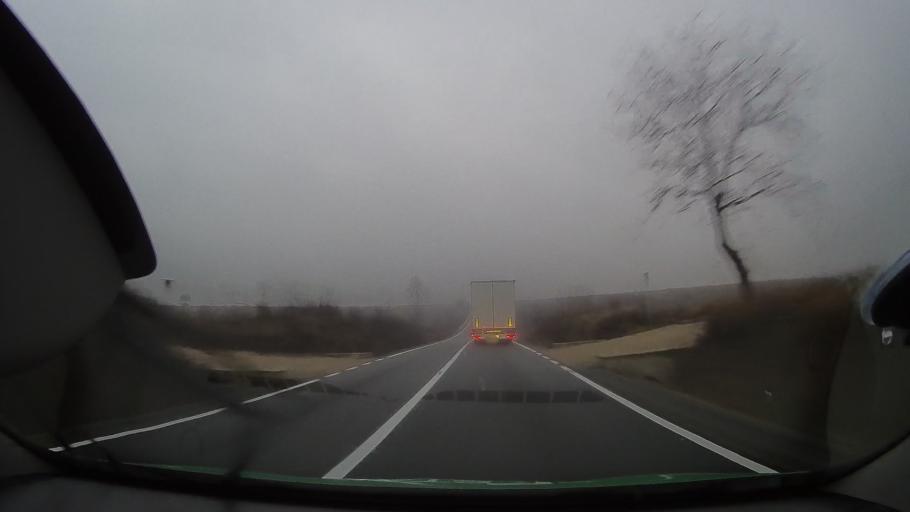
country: RO
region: Bihor
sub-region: Comuna Olcea
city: Olcea
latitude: 46.6585
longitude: 21.9613
